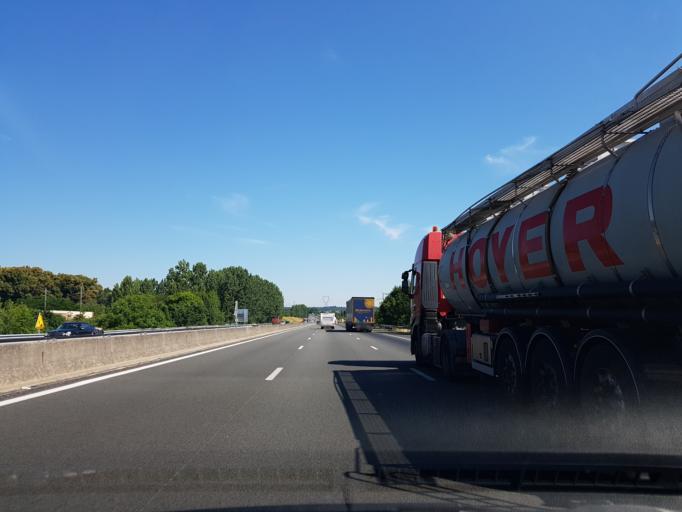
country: FR
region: Picardie
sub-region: Departement de l'Oise
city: Longueil-Sainte-Marie
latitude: 49.3668
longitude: 2.7041
